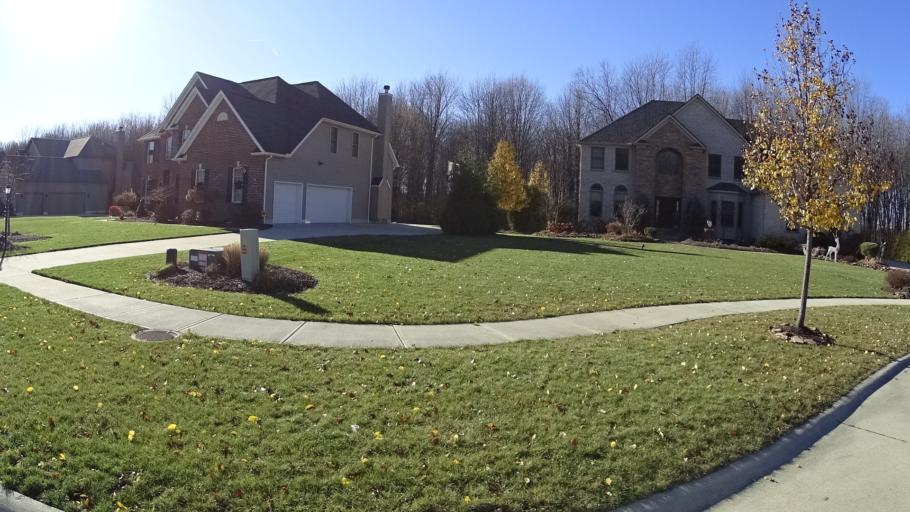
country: US
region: Ohio
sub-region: Lorain County
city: Avon Center
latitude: 41.4486
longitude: -81.9758
